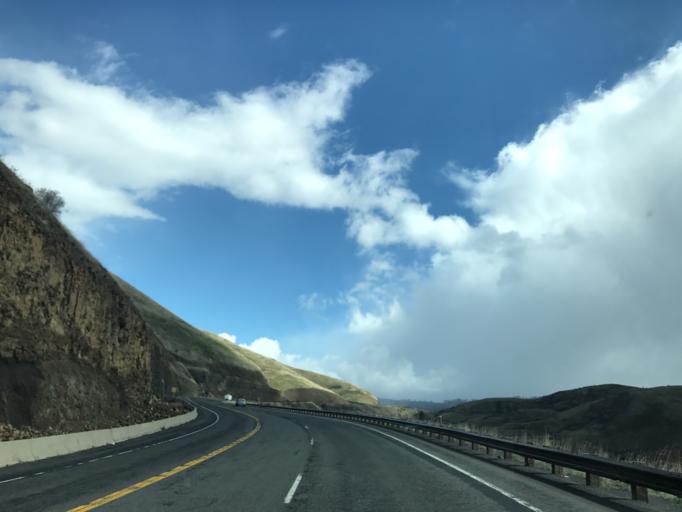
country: US
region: Idaho
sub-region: Idaho County
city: Grangeville
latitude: 45.8234
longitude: -116.2613
